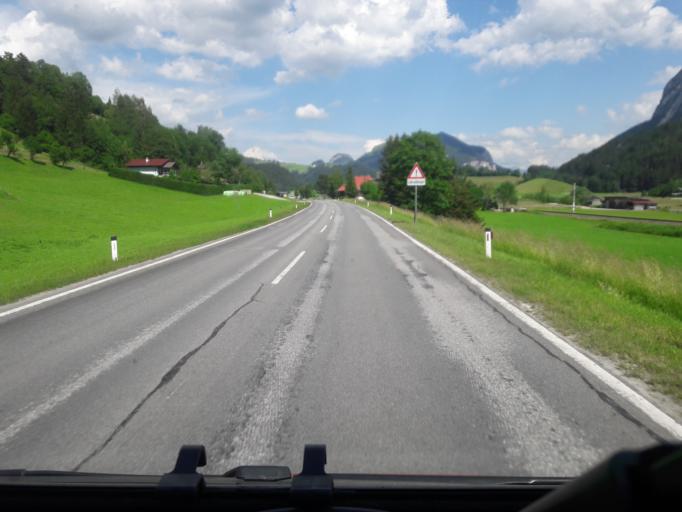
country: AT
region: Styria
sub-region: Politischer Bezirk Liezen
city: Tauplitz
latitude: 47.5523
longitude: 13.9872
